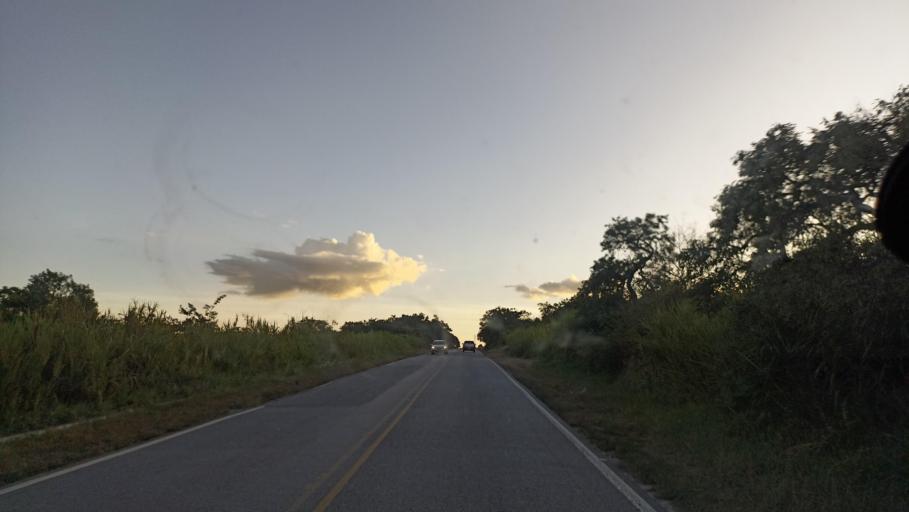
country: BR
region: Minas Gerais
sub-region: Sao Joao Del Rei
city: Sao Joao del Rei
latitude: -21.2316
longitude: -44.3853
